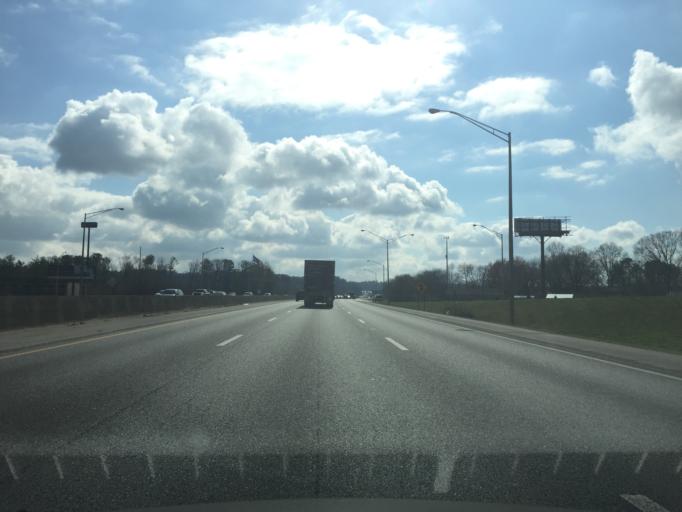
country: US
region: Georgia
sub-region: Catoosa County
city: Indian Springs
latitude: 34.9892
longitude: -85.2035
